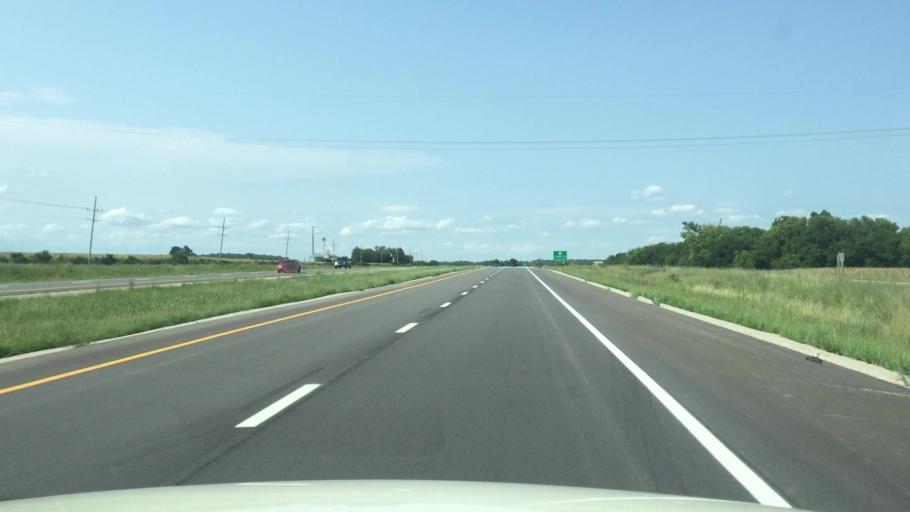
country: US
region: Kansas
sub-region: Linn County
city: La Cygne
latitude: 38.3229
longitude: -94.6774
